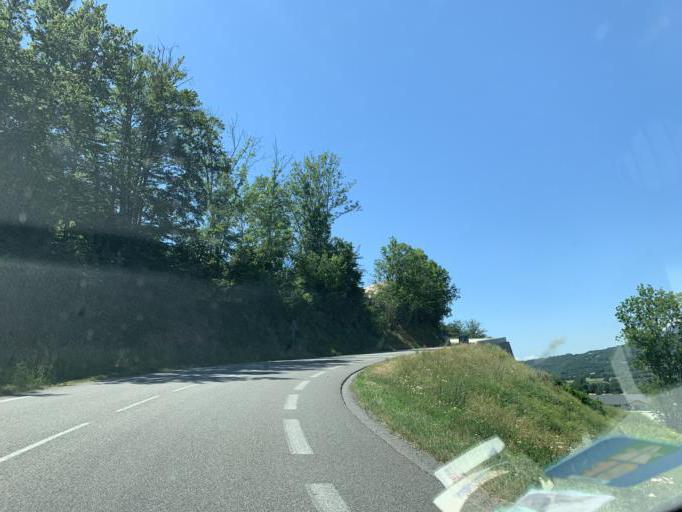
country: FR
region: Provence-Alpes-Cote d'Azur
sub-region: Departement des Hautes-Alpes
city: Saint-Bonnet-en-Champsaur
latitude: 44.6381
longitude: 6.1417
